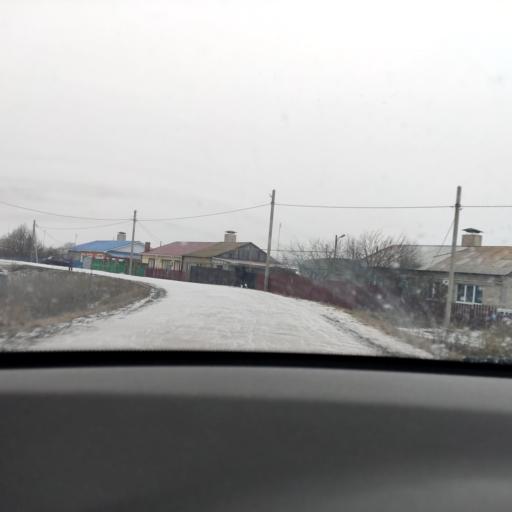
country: RU
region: Samara
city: Krasnoarmeyskoye
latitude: 52.9000
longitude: 50.0392
